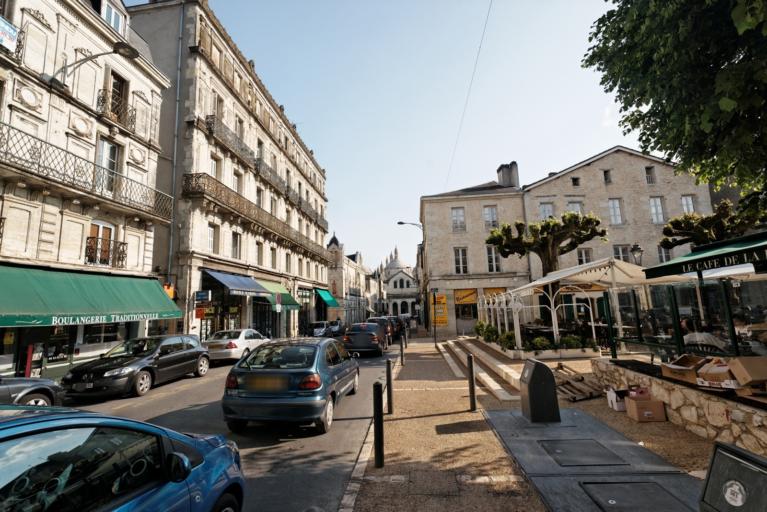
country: FR
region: Aquitaine
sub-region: Departement de la Dordogne
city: Perigueux
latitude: 45.1855
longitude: 0.7228
